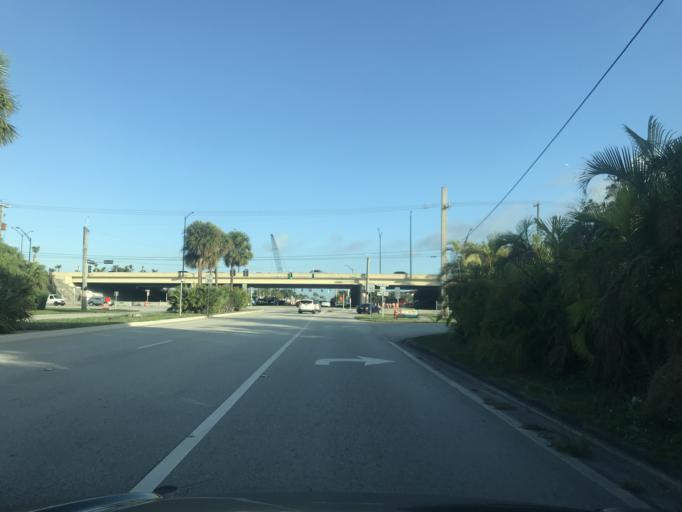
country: US
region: Florida
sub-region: Broward County
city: Pine Island Ridge
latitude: 26.1201
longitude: -80.3289
